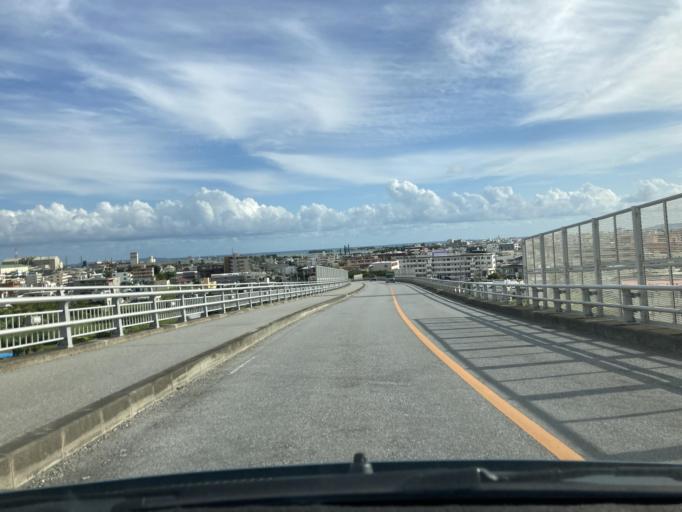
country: JP
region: Okinawa
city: Okinawa
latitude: 26.3387
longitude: 127.8343
